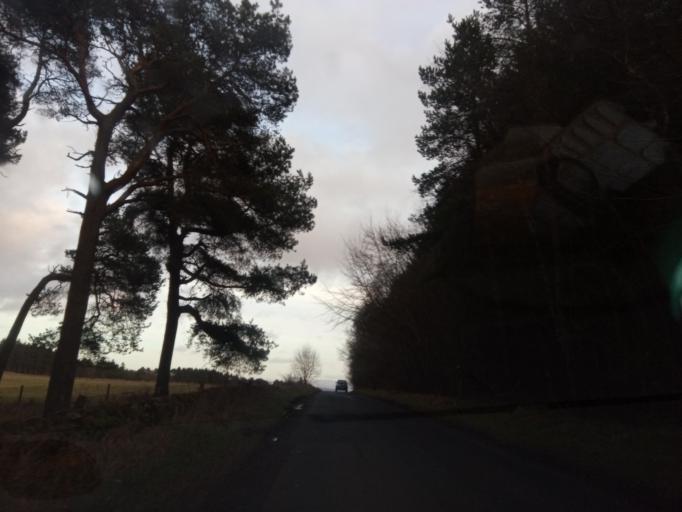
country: GB
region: Scotland
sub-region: The Scottish Borders
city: Selkirk
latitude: 55.5539
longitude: -2.7827
